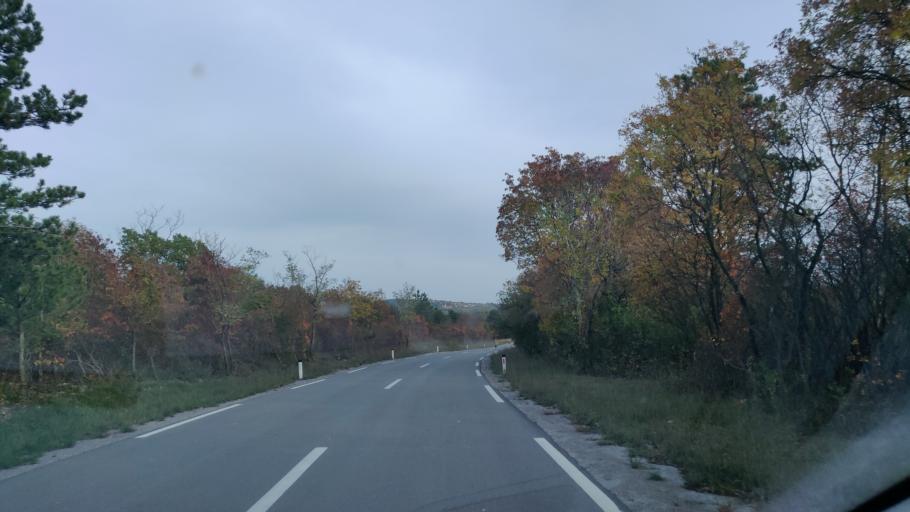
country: SI
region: Miren-Kostanjevica
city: Miren
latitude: 45.8490
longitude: 13.6134
